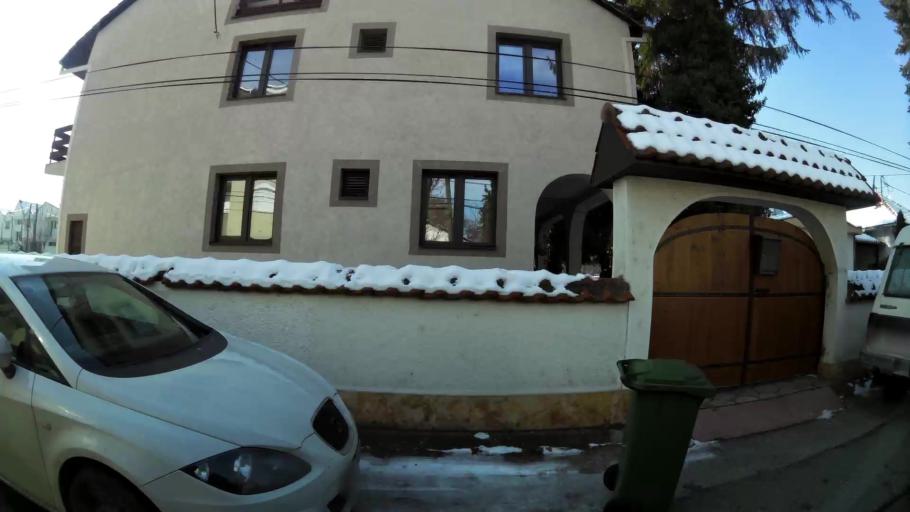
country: MK
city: Krushopek
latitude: 42.0048
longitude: 21.3697
